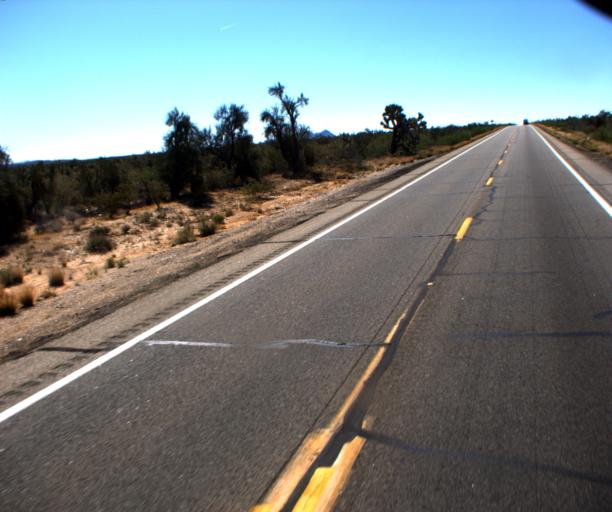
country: US
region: Arizona
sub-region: Yavapai County
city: Bagdad
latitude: 34.2930
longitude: -113.1125
